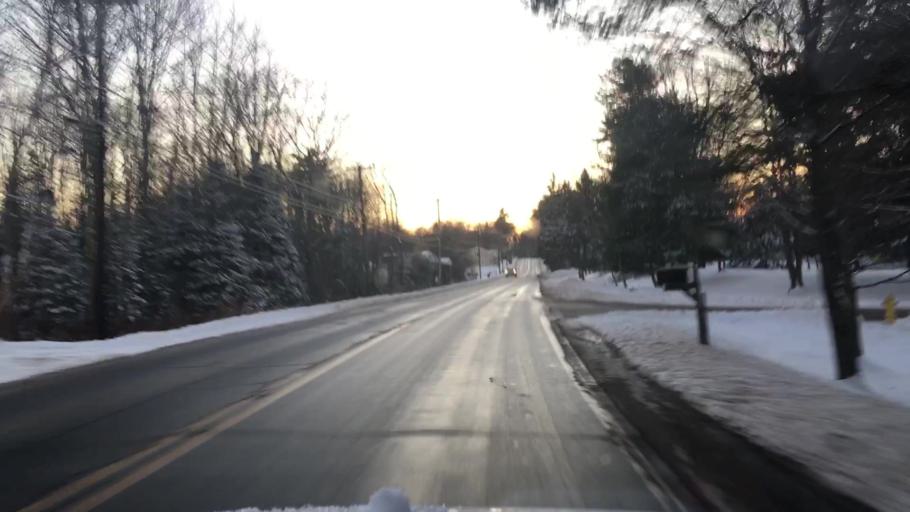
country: US
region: Maine
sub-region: Cumberland County
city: Brunswick
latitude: 43.9415
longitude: -69.9307
